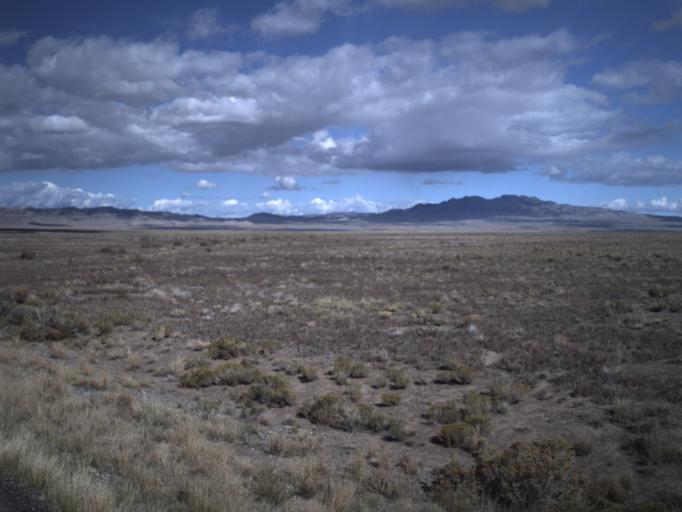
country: US
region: Utah
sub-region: Beaver County
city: Milford
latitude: 38.5307
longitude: -113.6773
